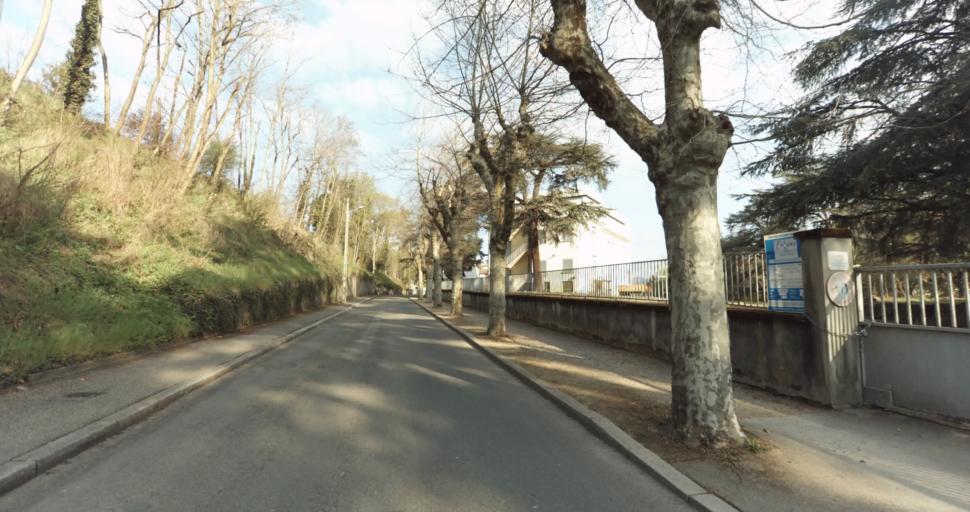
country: FR
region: Rhone-Alpes
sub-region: Departement du Rhone
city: Tarare
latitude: 45.8893
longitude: 4.4425
